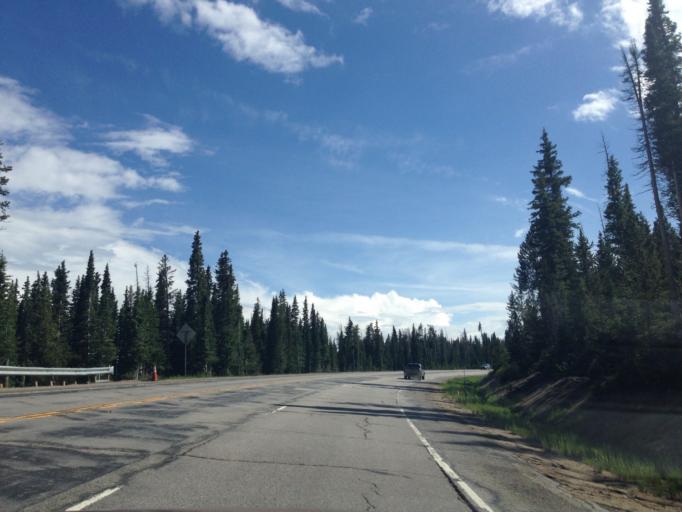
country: US
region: Colorado
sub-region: Routt County
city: Steamboat Springs
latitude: 40.3863
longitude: -106.6099
